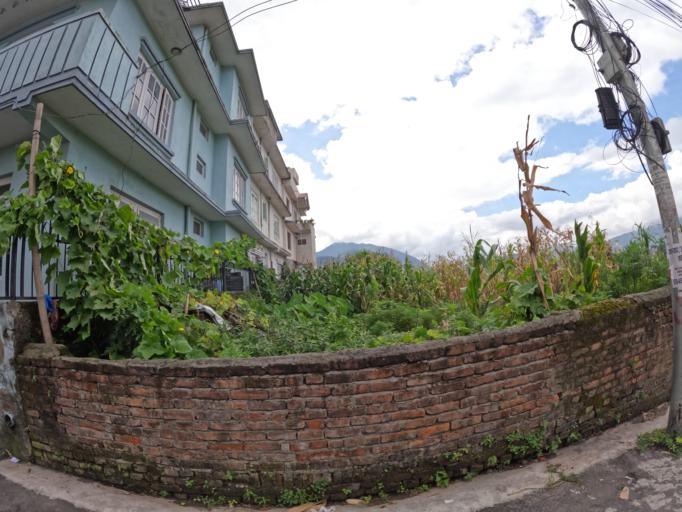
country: NP
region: Central Region
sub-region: Bagmati Zone
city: Kathmandu
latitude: 27.7437
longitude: 85.3176
